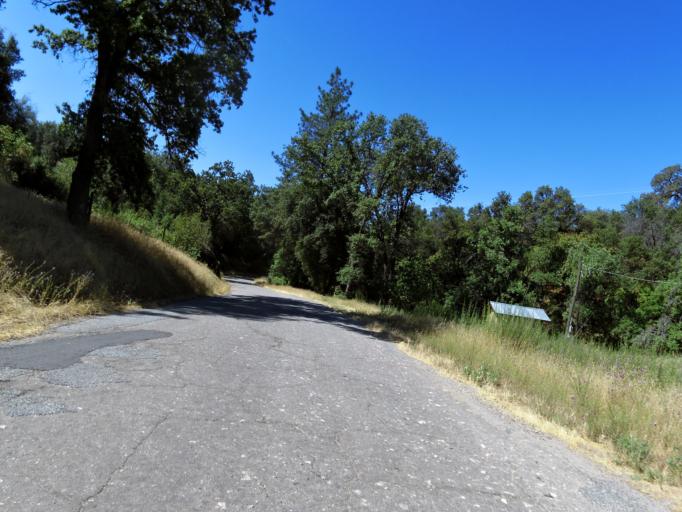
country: US
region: California
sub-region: Fresno County
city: Auberry
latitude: 37.1889
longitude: -119.4636
